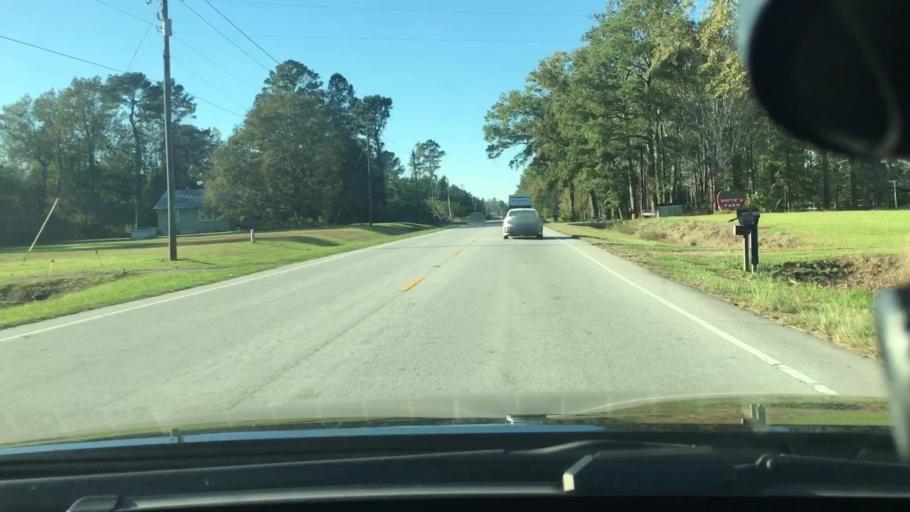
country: US
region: North Carolina
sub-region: Craven County
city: Vanceboro
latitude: 35.2419
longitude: -77.0803
